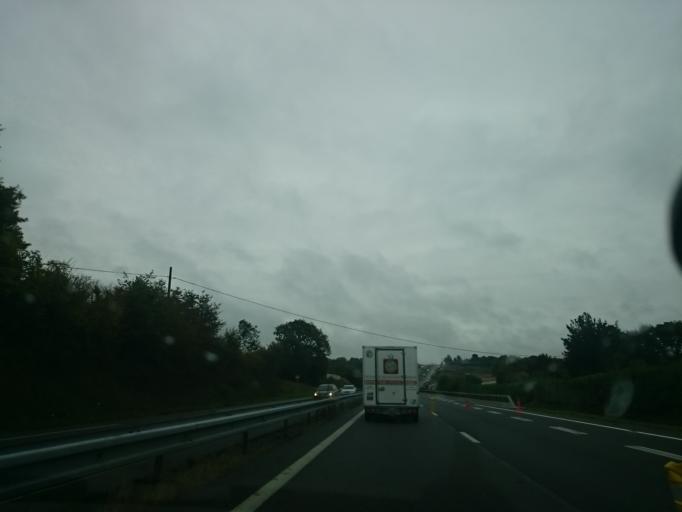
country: FR
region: Brittany
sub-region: Departement du Morbihan
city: Muzillac
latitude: 47.5494
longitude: -2.4740
